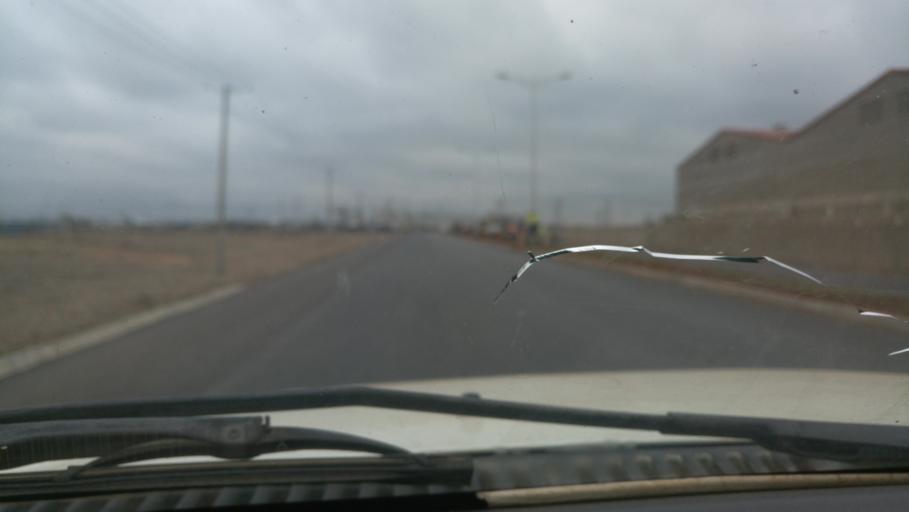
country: KE
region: Nairobi Area
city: Pumwani
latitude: -1.3429
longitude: 36.8797
